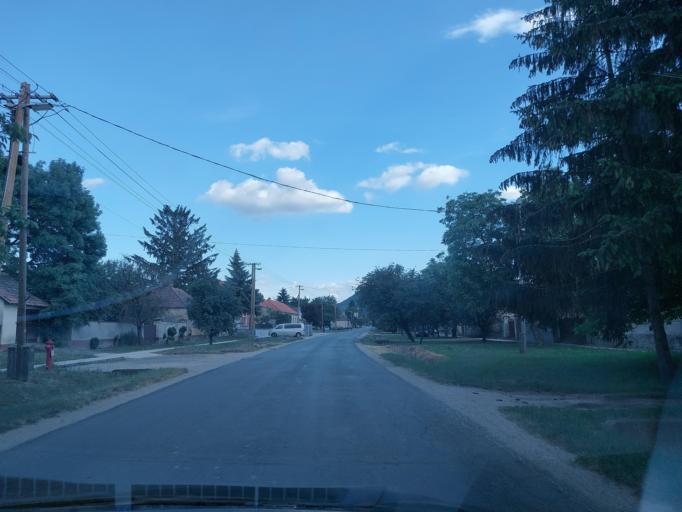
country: HU
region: Veszprem
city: Devecser
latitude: 47.1719
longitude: 17.3585
